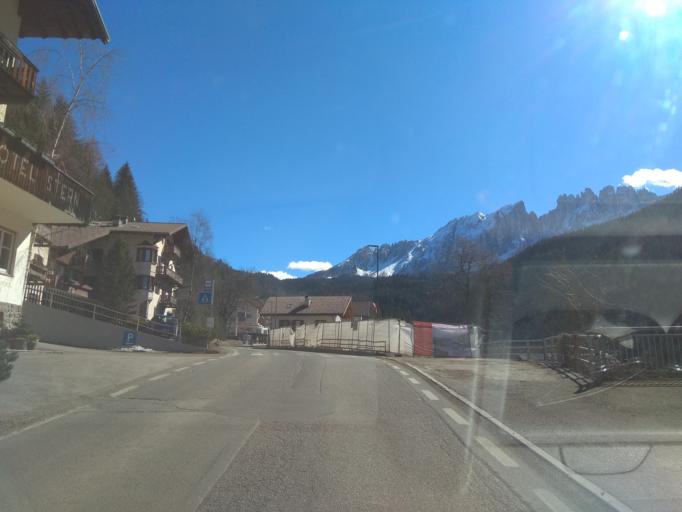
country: IT
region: Trentino-Alto Adige
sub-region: Bolzano
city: Nova Levante
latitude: 46.4267
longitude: 11.5484
